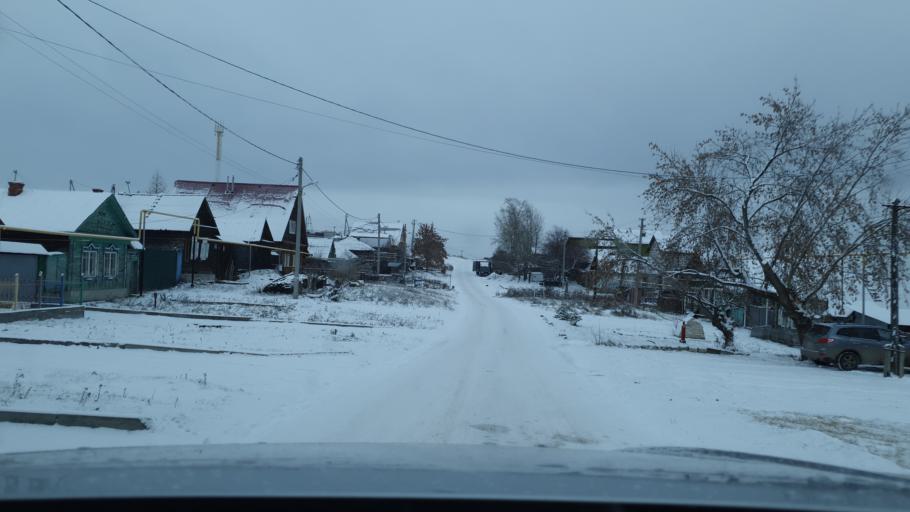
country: RU
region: Sverdlovsk
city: Istok
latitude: 56.7446
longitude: 60.6986
